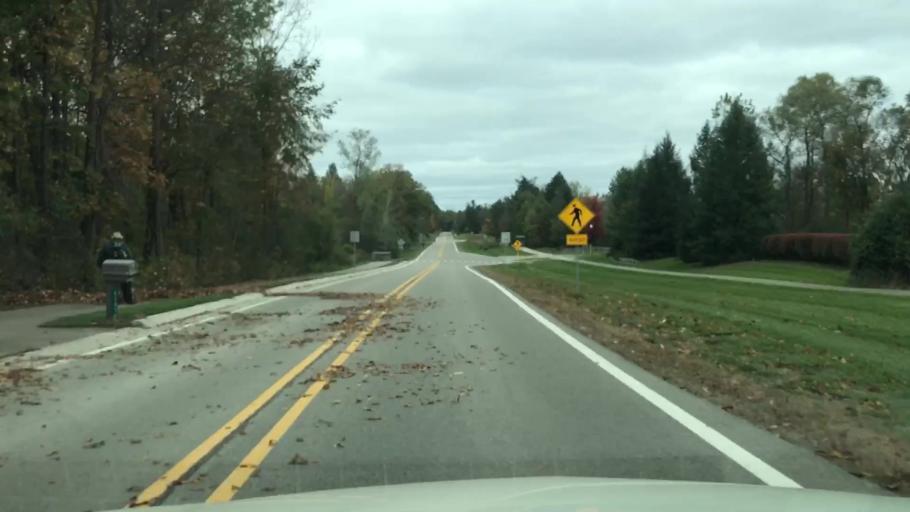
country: US
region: Michigan
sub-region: Oakland County
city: Rochester
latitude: 42.7041
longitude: -83.1242
